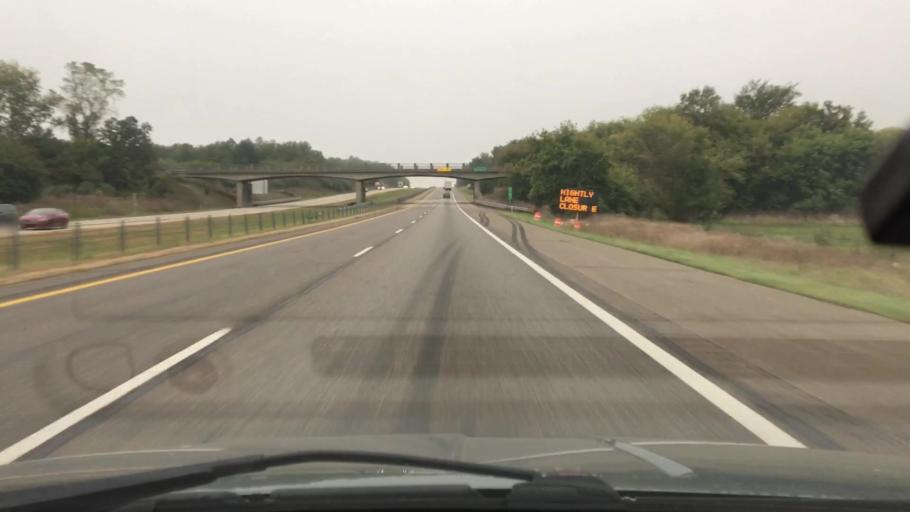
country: US
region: Michigan
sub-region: Calhoun County
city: Albion
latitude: 42.2836
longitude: -84.8261
